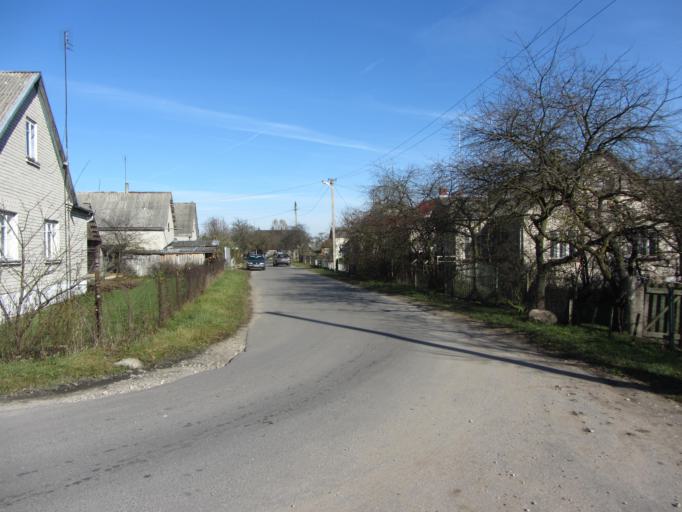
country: LT
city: Eisiskes
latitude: 54.1634
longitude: 25.0009
